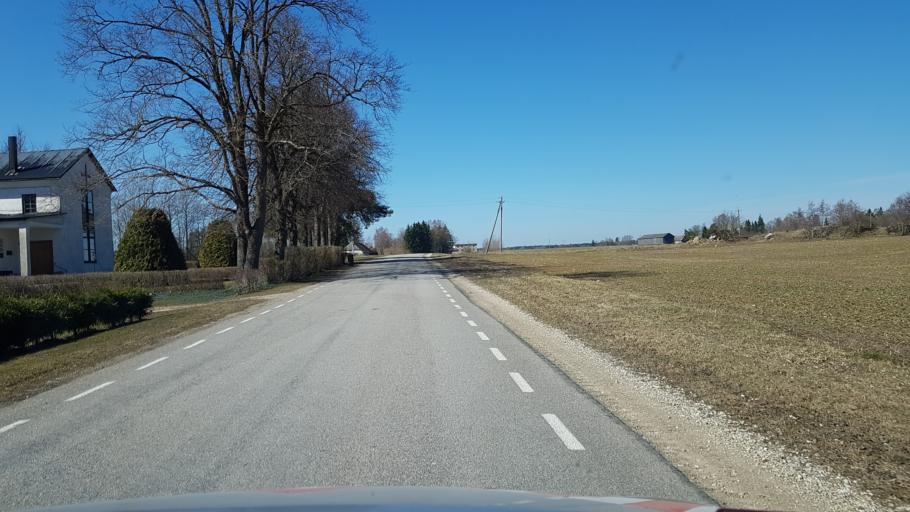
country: EE
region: Laeaene-Virumaa
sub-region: Vaeike-Maarja vald
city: Vaike-Maarja
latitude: 59.1091
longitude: 26.3776
